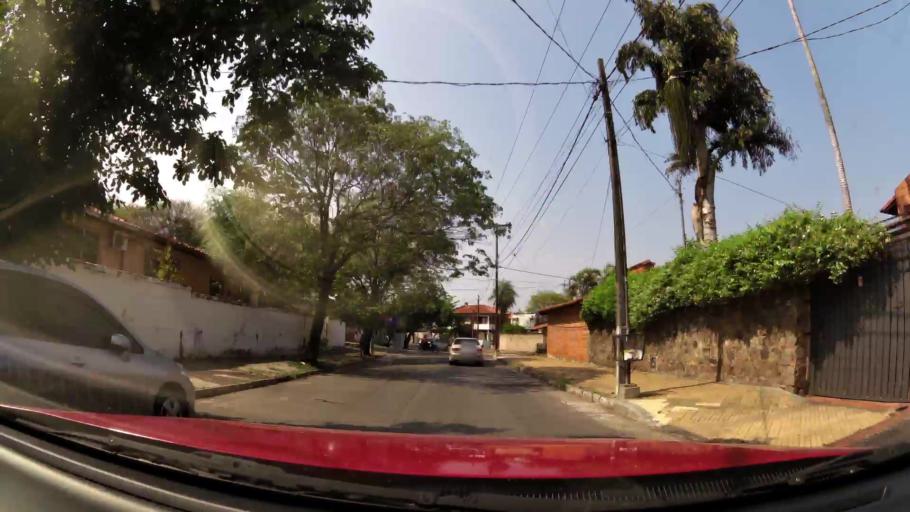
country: PY
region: Asuncion
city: Asuncion
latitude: -25.2939
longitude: -57.6590
